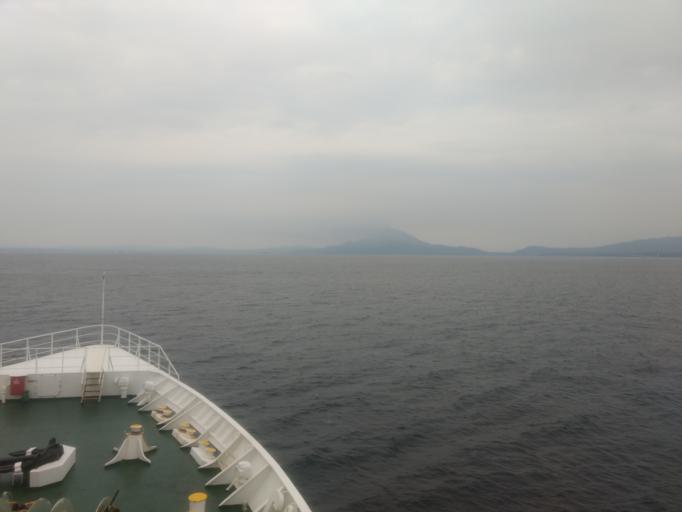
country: JP
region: Kagoshima
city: Tarumizu
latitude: 31.3908
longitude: 130.6624
